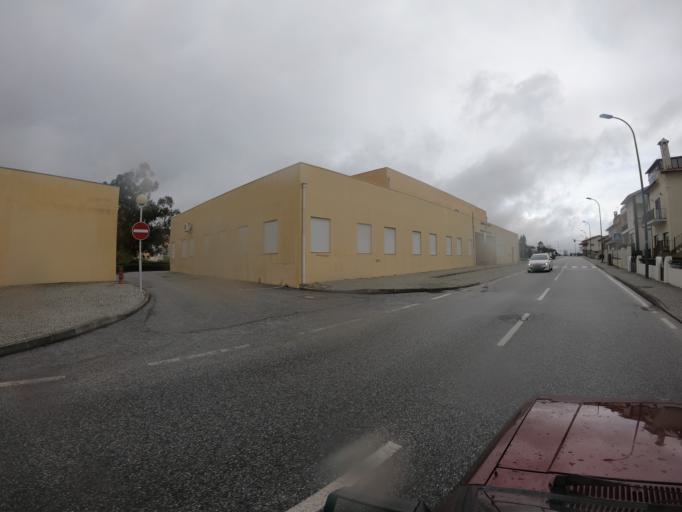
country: PT
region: Guarda
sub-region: Celorico da Beira
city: Celorico da Beira
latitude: 40.6291
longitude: -7.3975
